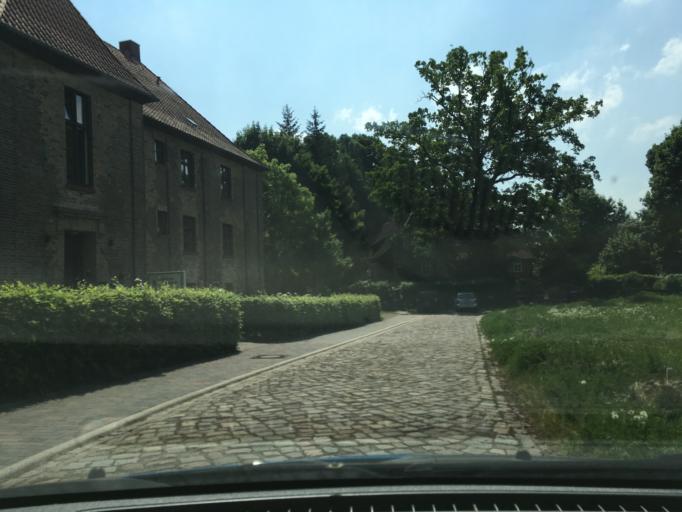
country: DE
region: Lower Saxony
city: Lueneburg
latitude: 53.2487
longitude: 10.3949
